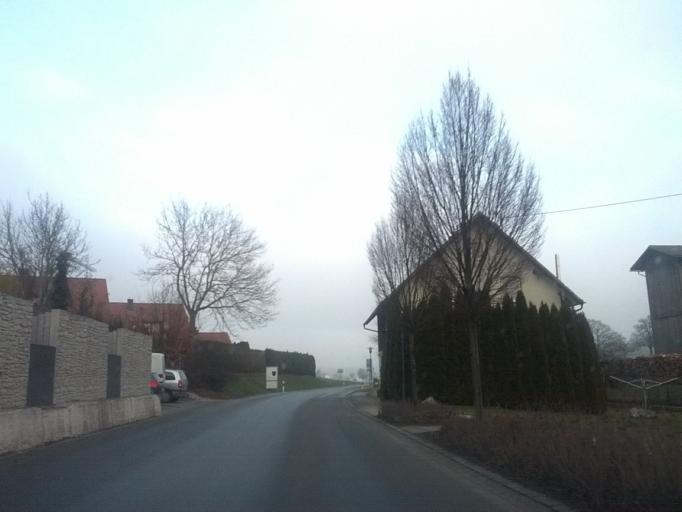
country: DE
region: Baden-Wuerttemberg
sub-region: Tuebingen Region
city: Steinhausen an der Rottum
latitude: 47.9772
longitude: 9.9430
